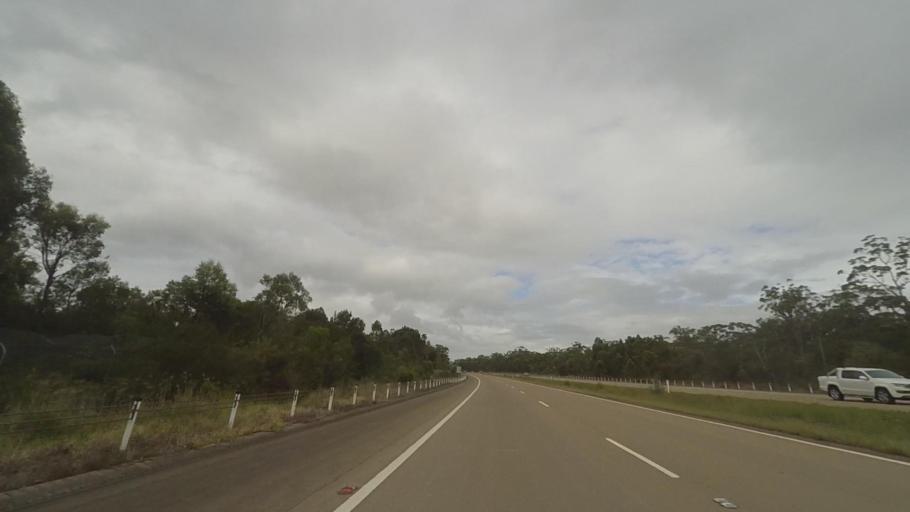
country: AU
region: New South Wales
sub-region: Port Stephens Shire
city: Medowie
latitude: -32.6461
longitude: 151.9225
